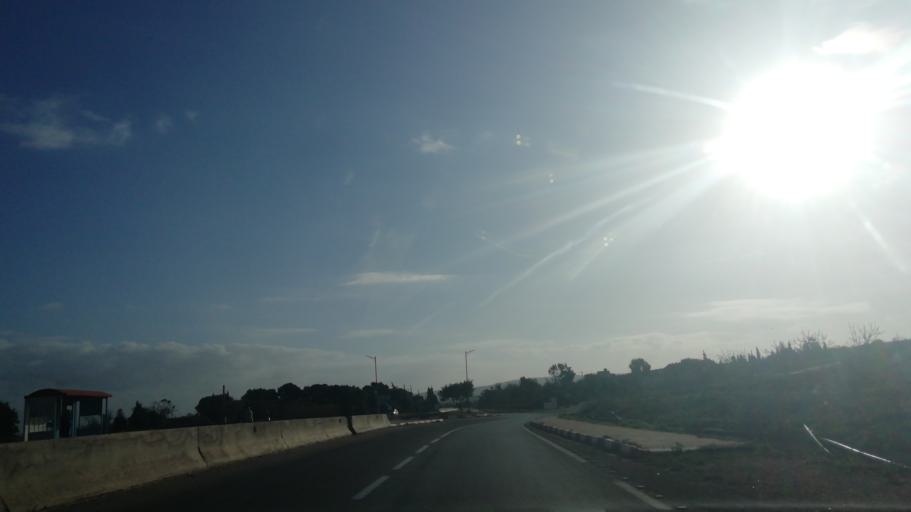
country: DZ
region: Mostaganem
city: Mostaganem
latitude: 36.1069
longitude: 0.3009
